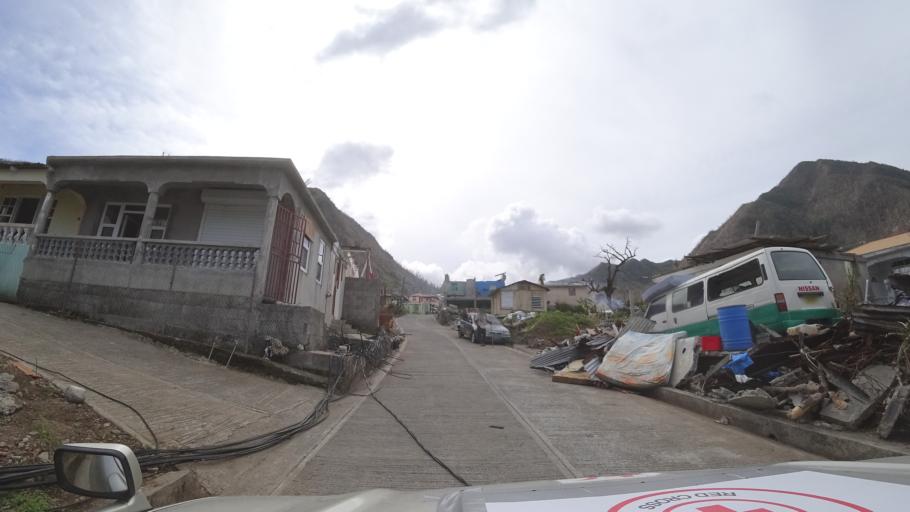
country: DM
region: Saint Patrick
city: Berekua
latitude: 15.2357
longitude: -61.3317
